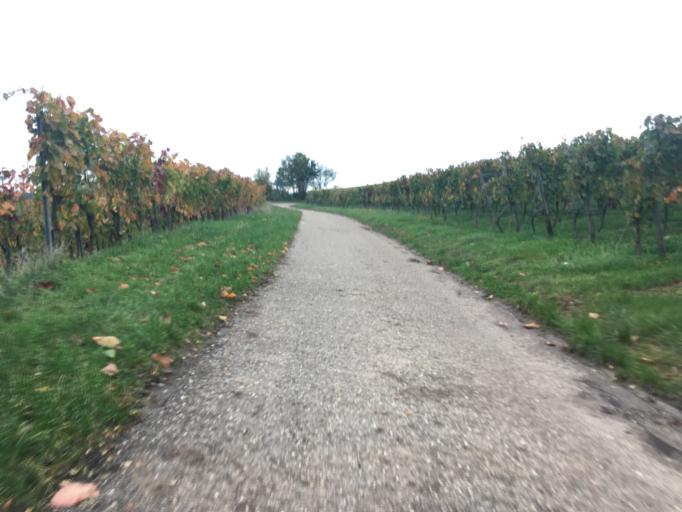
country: DE
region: Baden-Wuerttemberg
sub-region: Regierungsbezirk Stuttgart
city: Neckarwestheim
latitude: 49.0589
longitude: 9.1827
